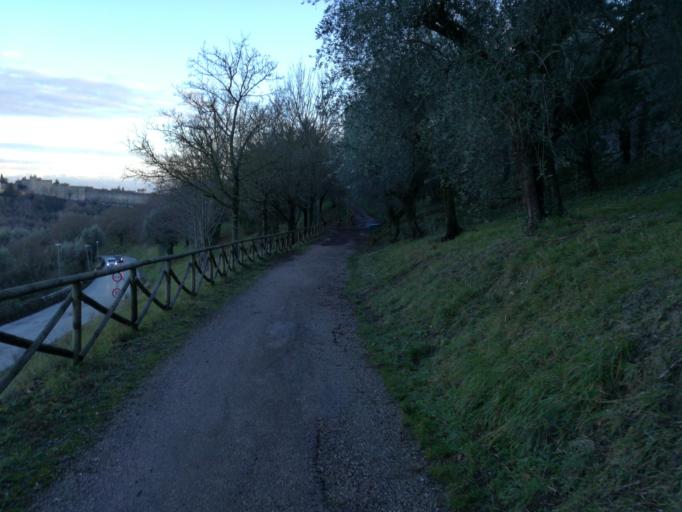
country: IT
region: Umbria
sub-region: Provincia di Perugia
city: Perugia
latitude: 43.1188
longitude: 12.3874
